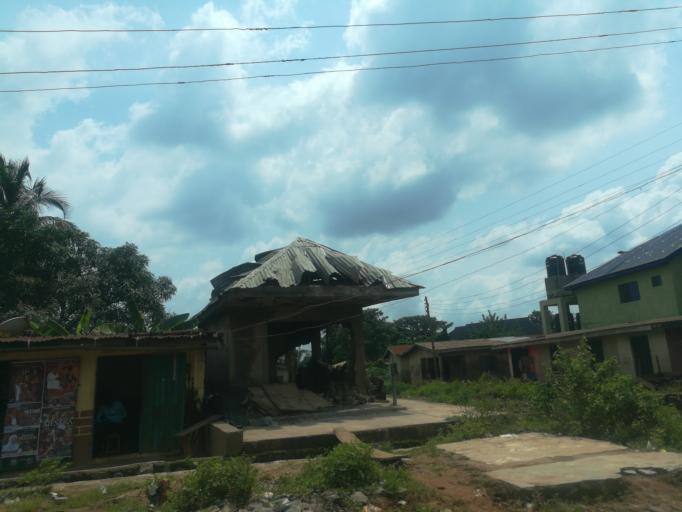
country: NG
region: Oyo
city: Ibadan
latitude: 7.4509
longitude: 3.9554
